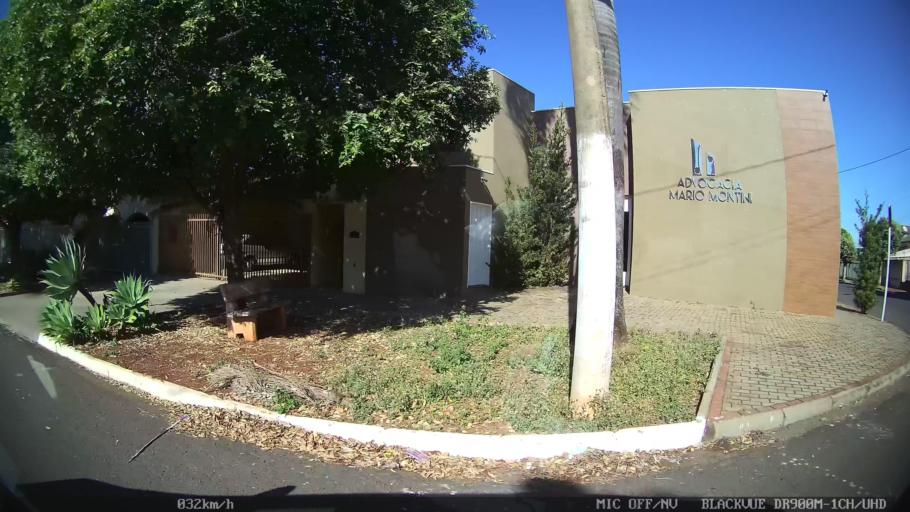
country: BR
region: Sao Paulo
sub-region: Olimpia
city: Olimpia
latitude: -20.7436
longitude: -48.9152
